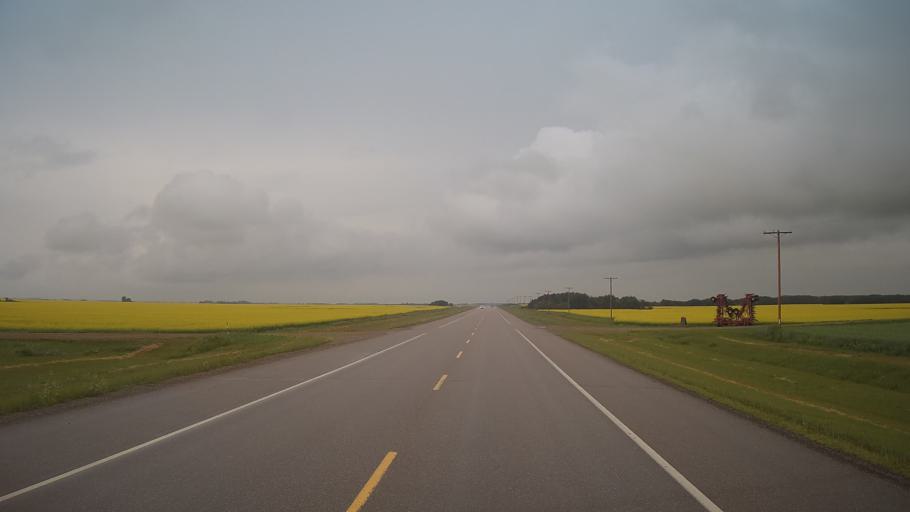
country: CA
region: Saskatchewan
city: Wilkie
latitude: 52.4244
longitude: -108.9049
